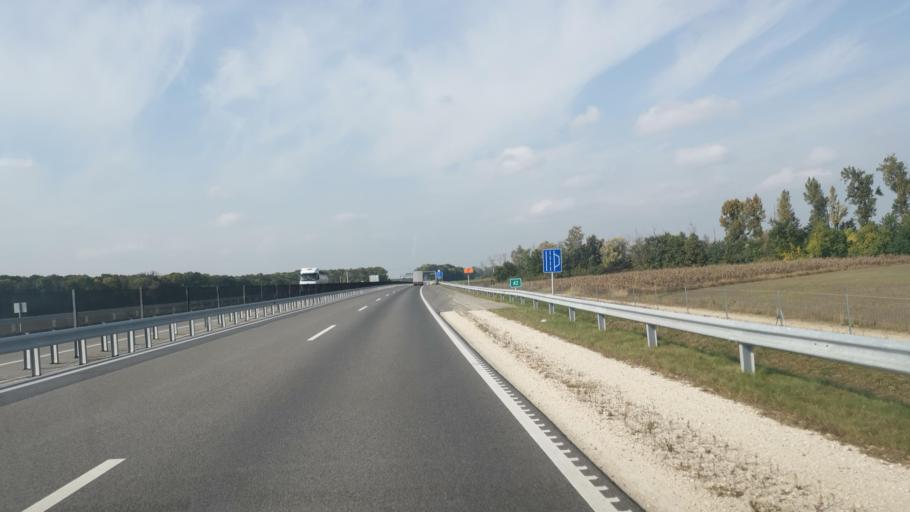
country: HU
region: Gyor-Moson-Sopron
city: Kapuvar
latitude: 47.5634
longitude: 17.0655
